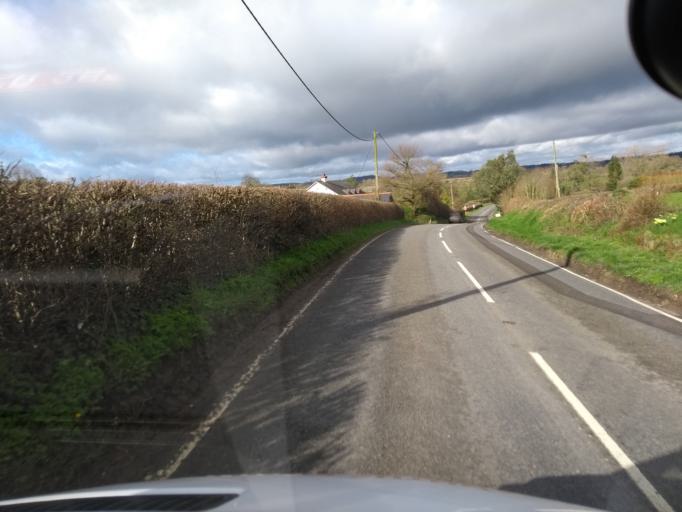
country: GB
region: England
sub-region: Somerset
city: Milborne Port
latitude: 50.9177
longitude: -2.4522
